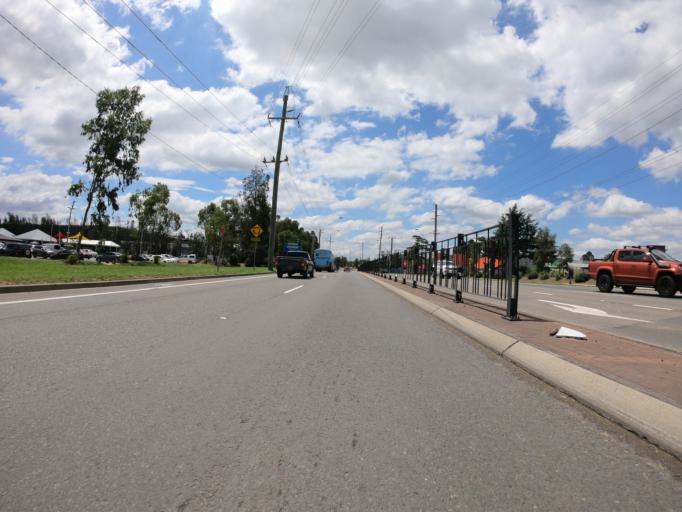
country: AU
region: New South Wales
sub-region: Penrith Municipality
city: Penrith
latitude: -33.7453
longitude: 150.6911
